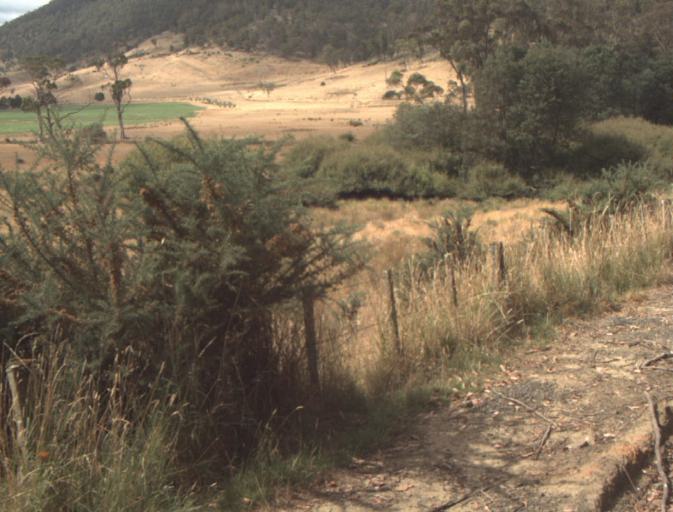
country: AU
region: Tasmania
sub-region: Northern Midlands
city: Evandale
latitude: -41.4895
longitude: 147.4356
